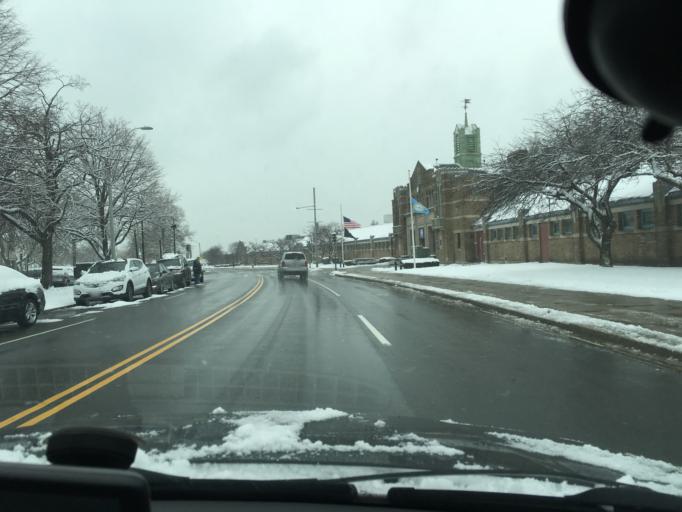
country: US
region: Massachusetts
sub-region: Suffolk County
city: South Boston
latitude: 42.3294
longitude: -71.0360
